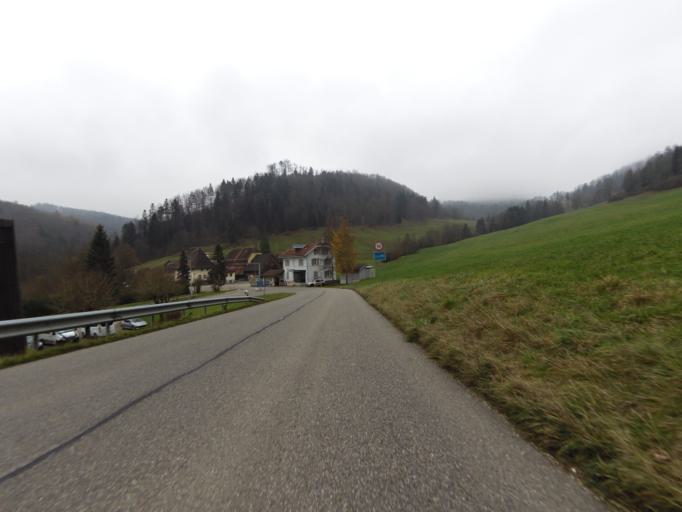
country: CH
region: Jura
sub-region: Delemont District
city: Bassecourt
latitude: 47.4185
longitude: 7.2433
